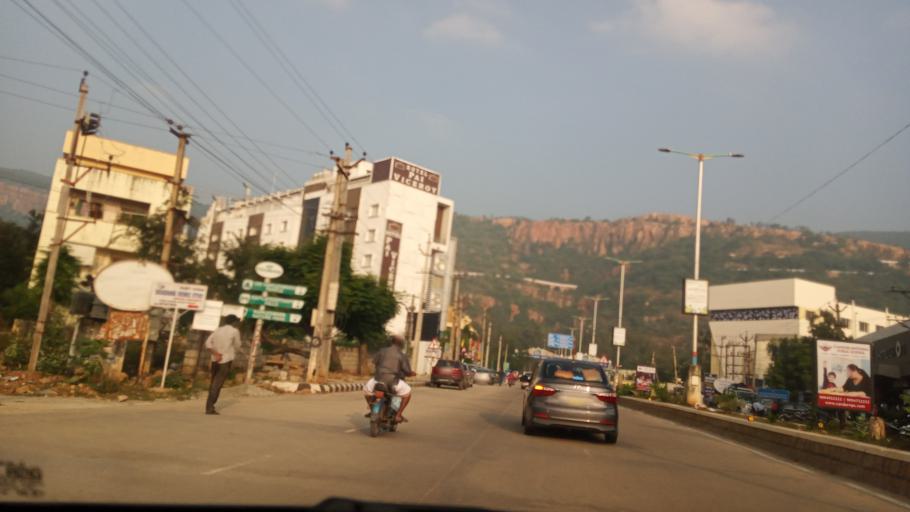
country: IN
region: Andhra Pradesh
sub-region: Chittoor
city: Akkarampalle
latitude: 13.6521
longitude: 79.4220
